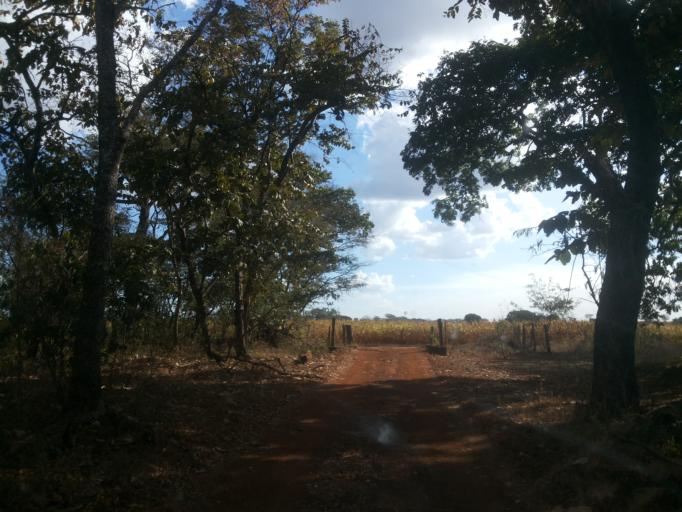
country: BR
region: Minas Gerais
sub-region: Capinopolis
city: Capinopolis
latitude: -18.6012
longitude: -49.4947
